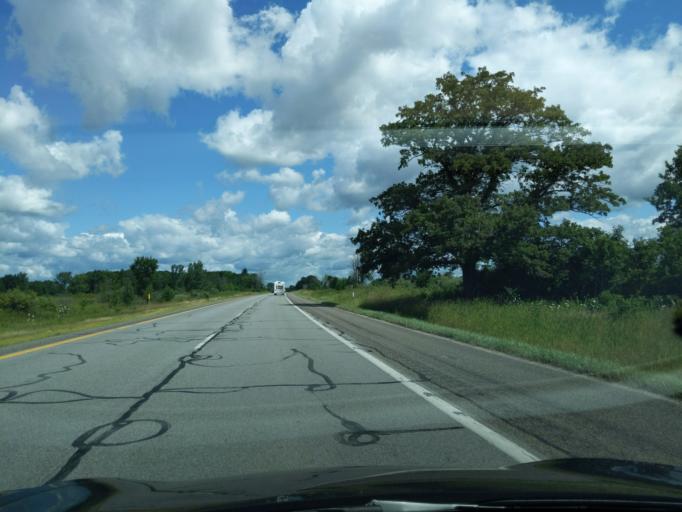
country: US
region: Michigan
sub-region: Clare County
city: Clare
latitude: 43.7467
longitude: -84.7578
